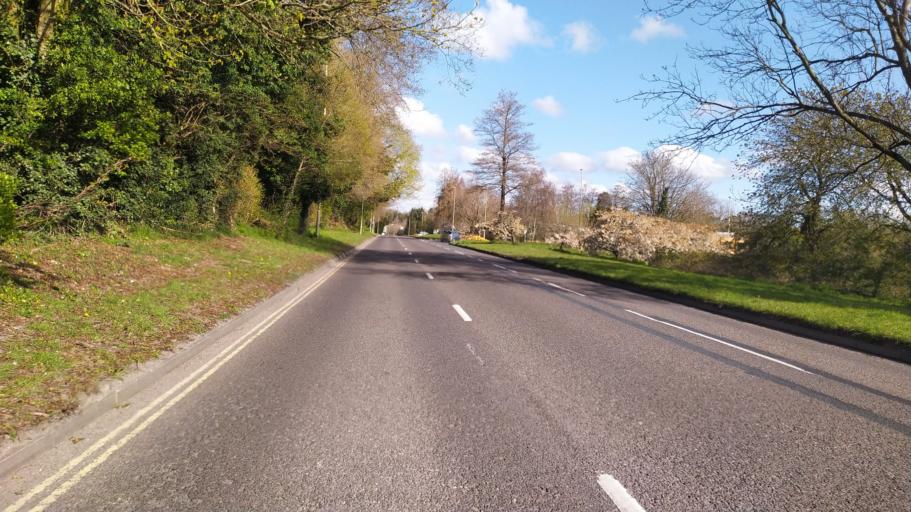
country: GB
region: England
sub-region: Hampshire
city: Andover
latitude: 51.2085
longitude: -1.4834
